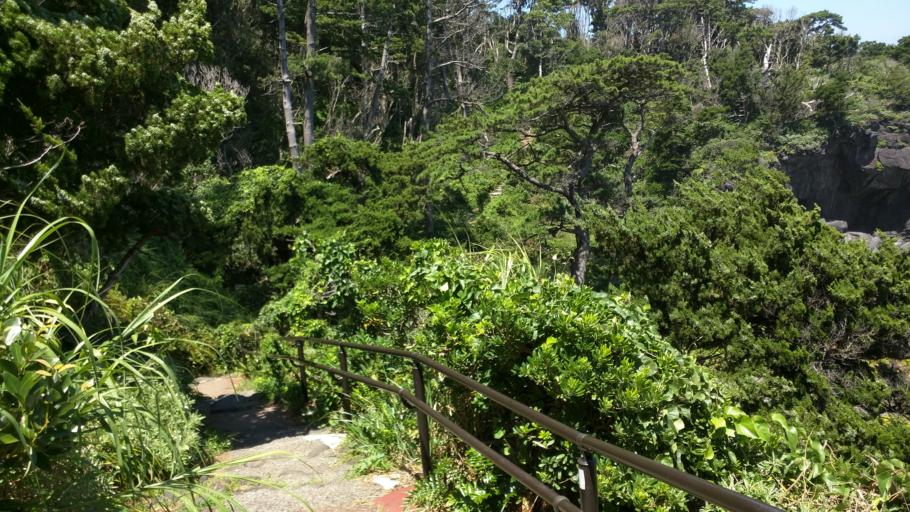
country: JP
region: Shizuoka
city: Ito
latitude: 34.8912
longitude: 139.1391
